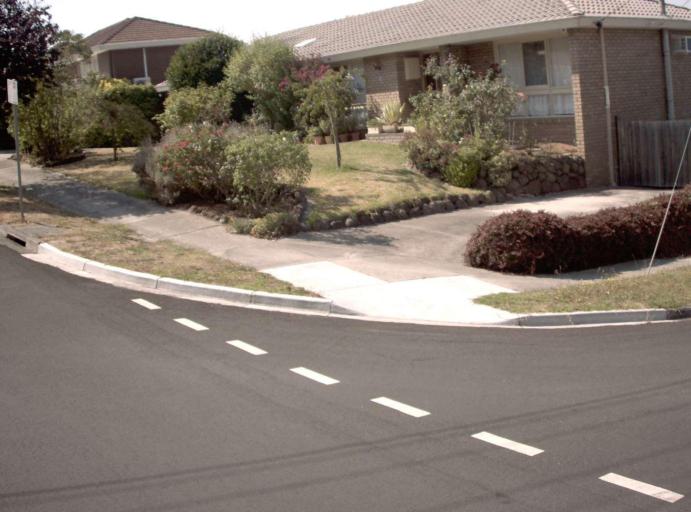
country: AU
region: Victoria
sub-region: Manningham
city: Doncaster
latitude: -37.7902
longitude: 145.1263
